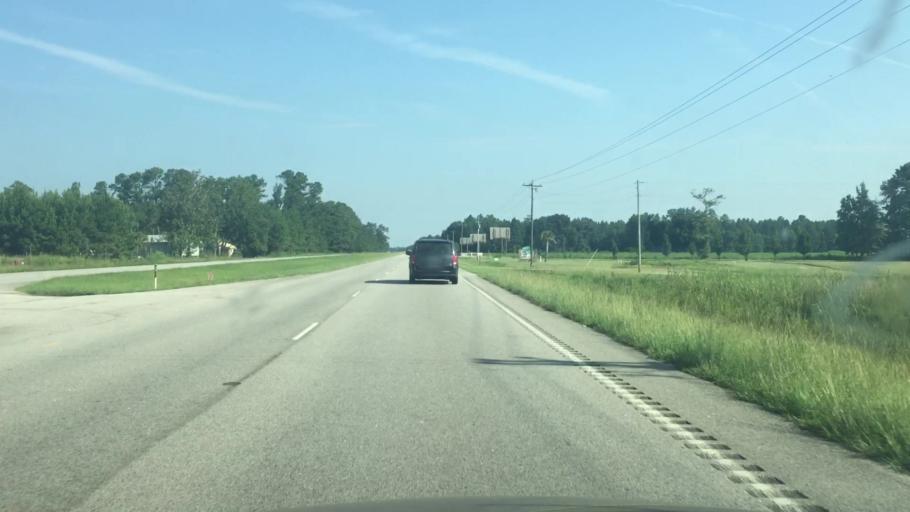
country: US
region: South Carolina
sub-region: Horry County
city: Little River
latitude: 33.9682
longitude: -78.7400
